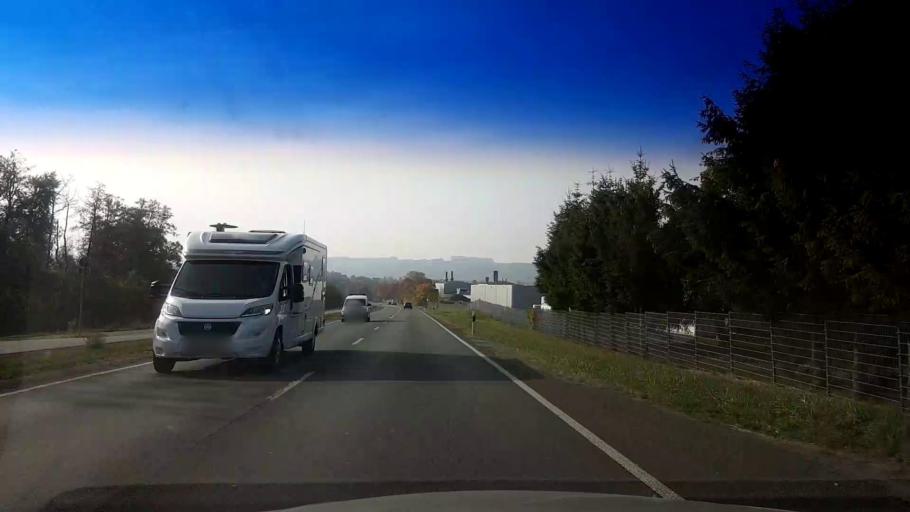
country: DE
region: Bavaria
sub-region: Upper Franconia
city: Himmelkron
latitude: 50.0702
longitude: 11.6070
